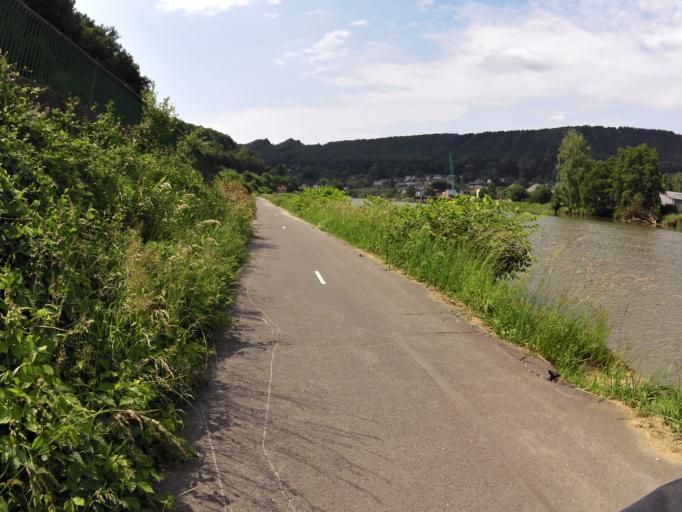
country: FR
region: Champagne-Ardenne
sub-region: Departement des Ardennes
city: Montherme
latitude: 49.8568
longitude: 4.7569
